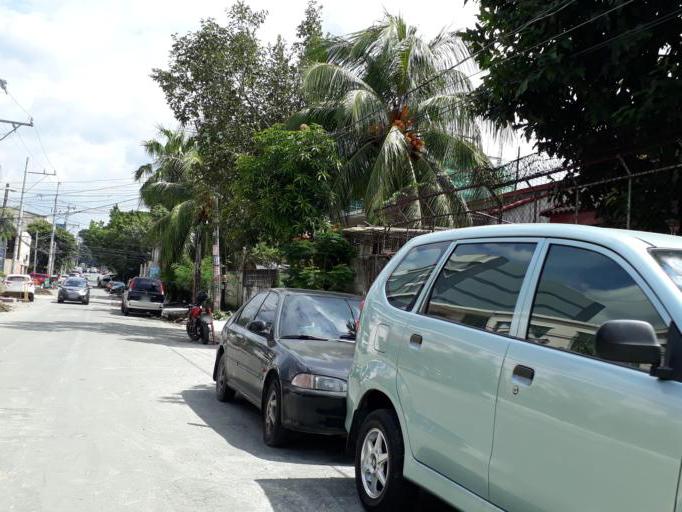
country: PH
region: Calabarzon
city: Del Monte
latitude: 14.6334
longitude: 120.9963
